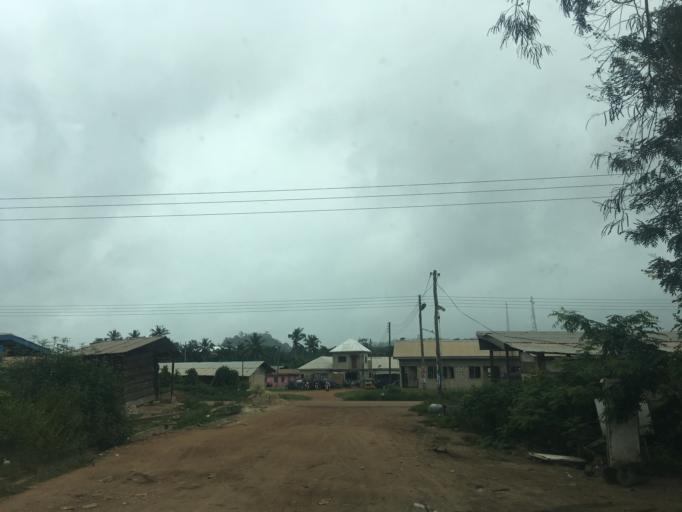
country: GH
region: Western
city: Wassa-Akropong
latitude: 5.8165
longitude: -2.4341
